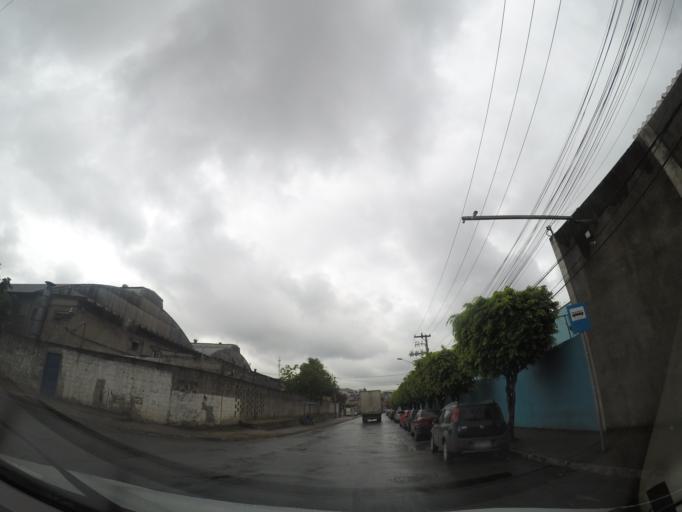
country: BR
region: Sao Paulo
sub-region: Guarulhos
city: Guarulhos
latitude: -23.4748
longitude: -46.4427
